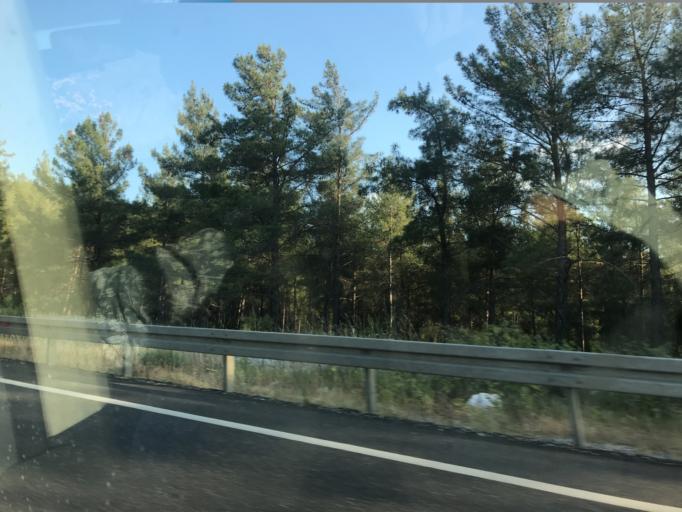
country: TR
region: Mugla
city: Ula
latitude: 37.0088
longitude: 28.5395
